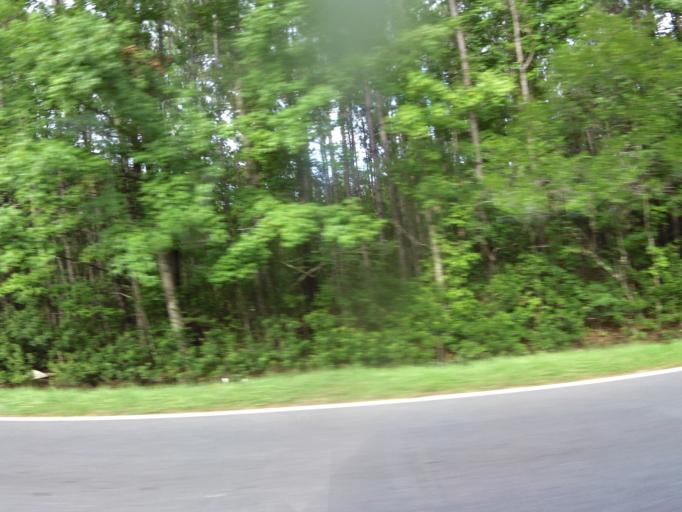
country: US
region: Florida
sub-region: Duval County
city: Jacksonville
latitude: 30.3829
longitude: -81.7510
